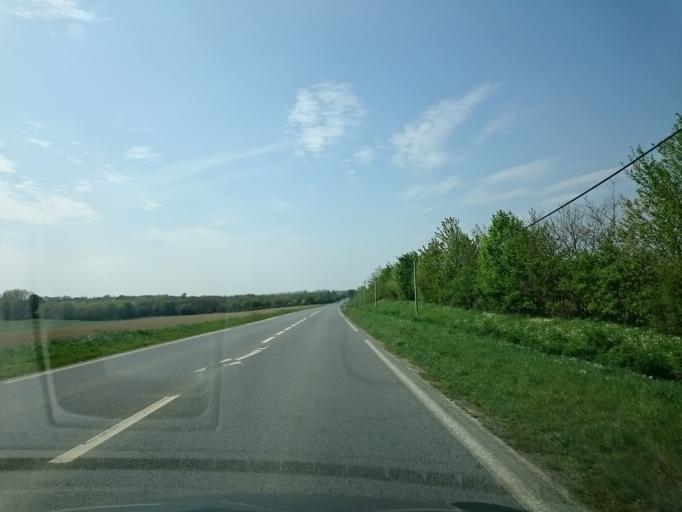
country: FR
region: Brittany
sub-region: Departement d'Ille-et-Vilaine
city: Chantepie
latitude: 48.0757
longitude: -1.5833
